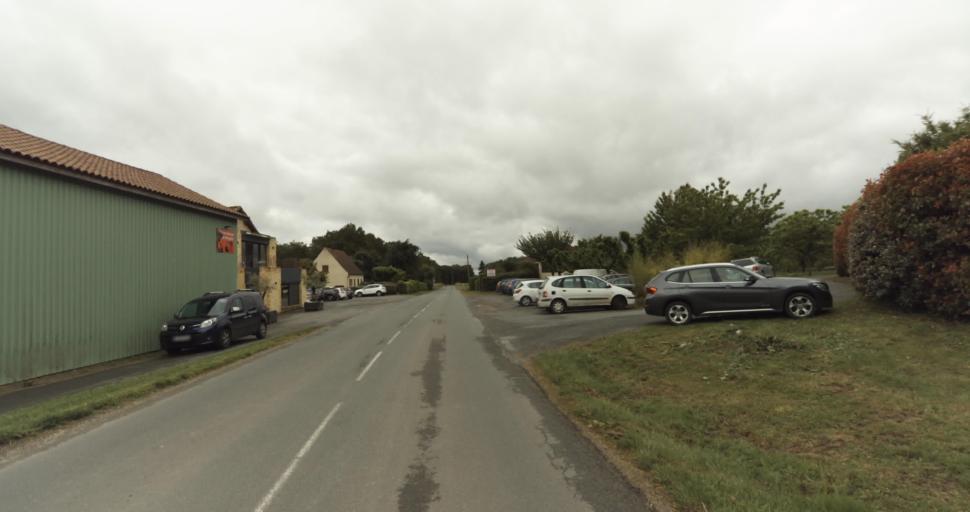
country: FR
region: Aquitaine
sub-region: Departement de la Dordogne
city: Belves
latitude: 44.6952
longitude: 0.9138
